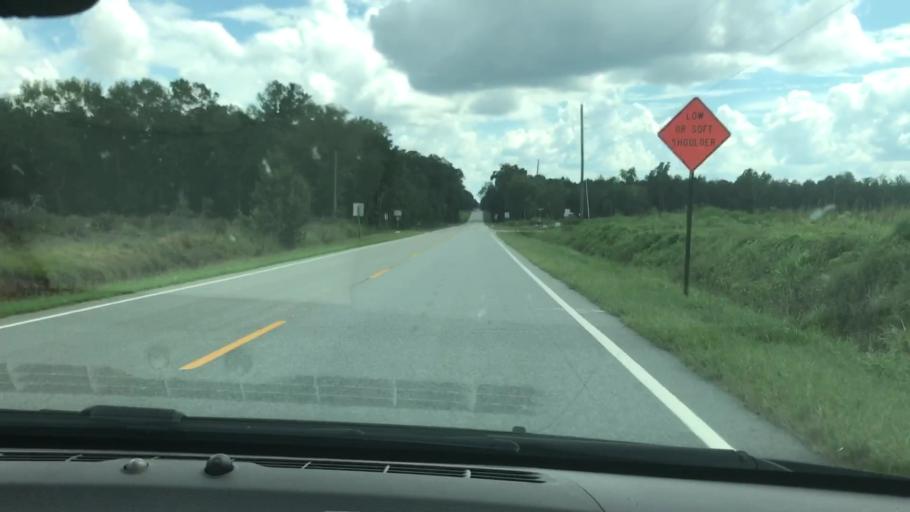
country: US
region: Georgia
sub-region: Quitman County
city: Georgetown
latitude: 31.7802
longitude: -85.0918
